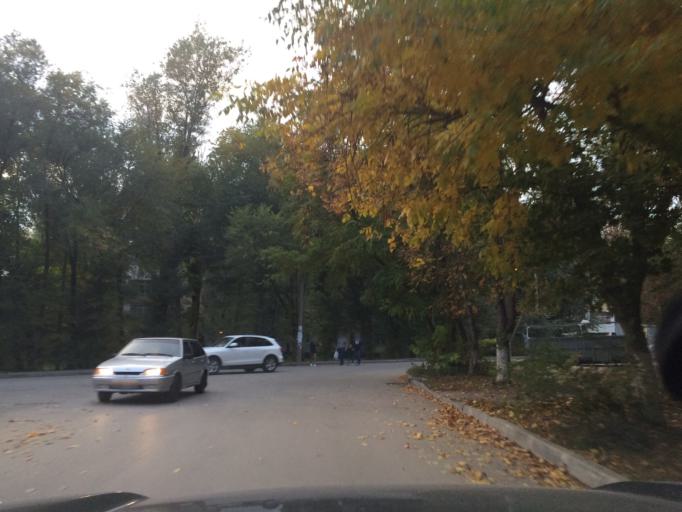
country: RU
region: Rostov
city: Rostov-na-Donu
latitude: 47.2017
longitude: 39.6183
